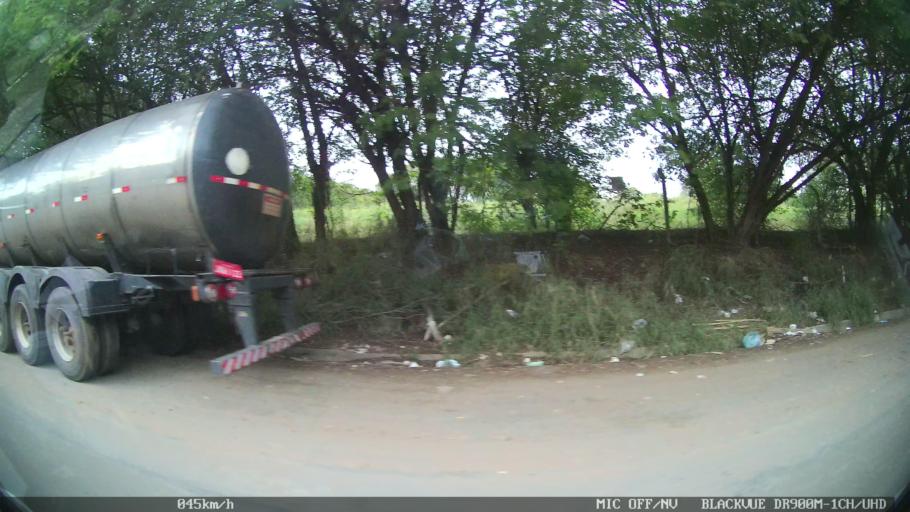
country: BR
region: Sao Paulo
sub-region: Americana
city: Americana
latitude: -22.6980
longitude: -47.3556
